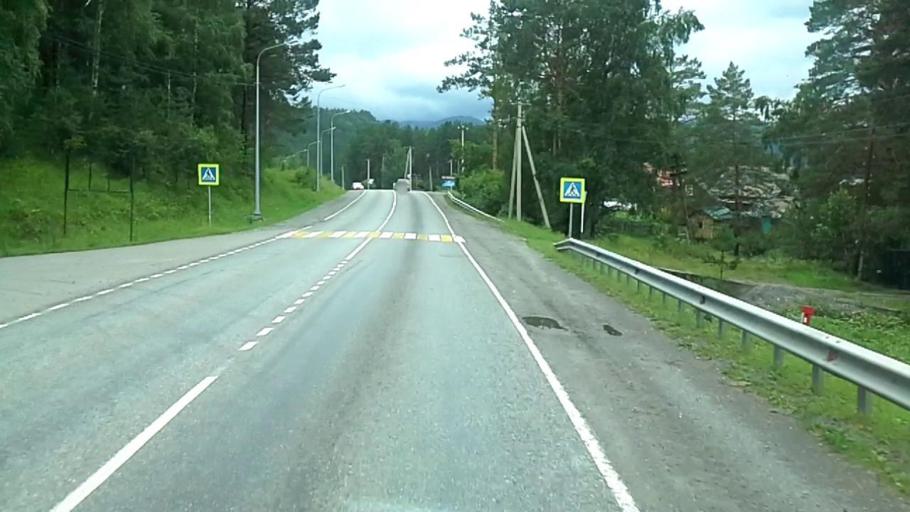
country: RU
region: Altay
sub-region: Mayminskiy Rayon
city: Manzherok
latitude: 51.8183
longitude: 85.7809
